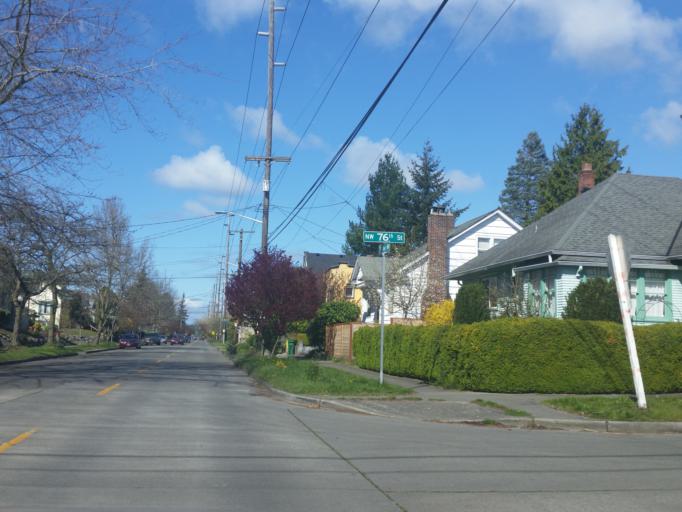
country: US
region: Washington
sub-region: King County
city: Shoreline
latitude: 47.6840
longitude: -122.3607
